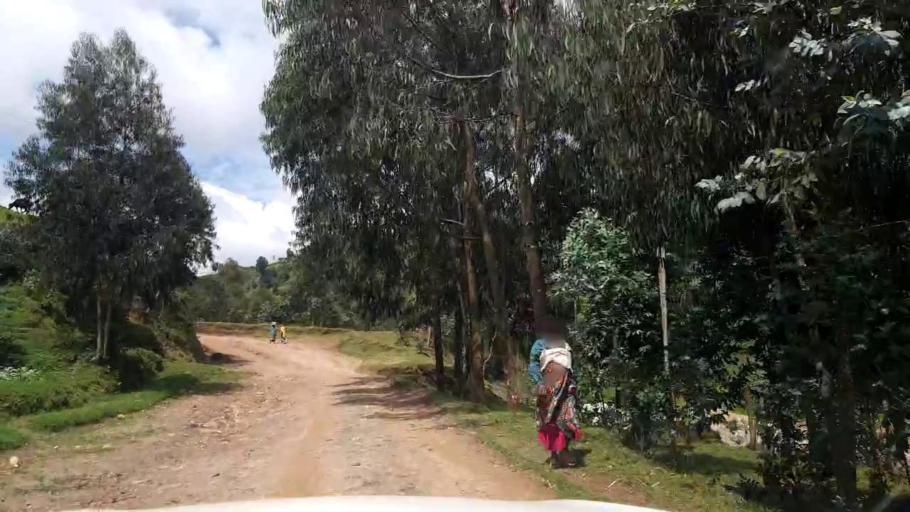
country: RW
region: Western Province
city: Kibuye
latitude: -1.9114
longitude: 29.4573
